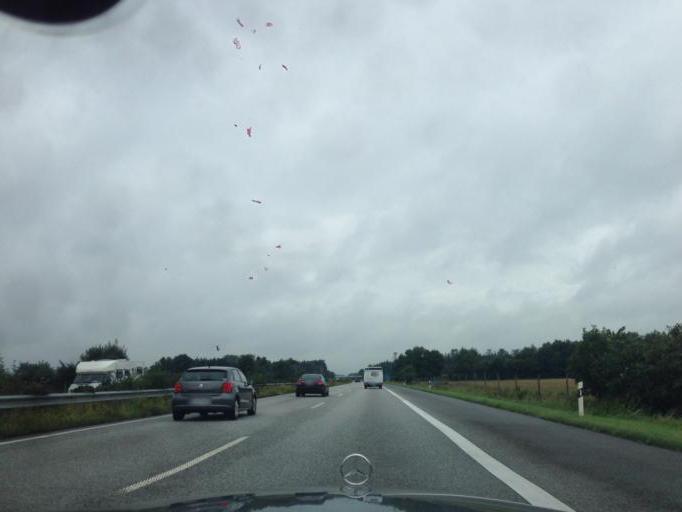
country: DE
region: Schleswig-Holstein
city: Gross Vollstedt
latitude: 54.2198
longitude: 9.8540
